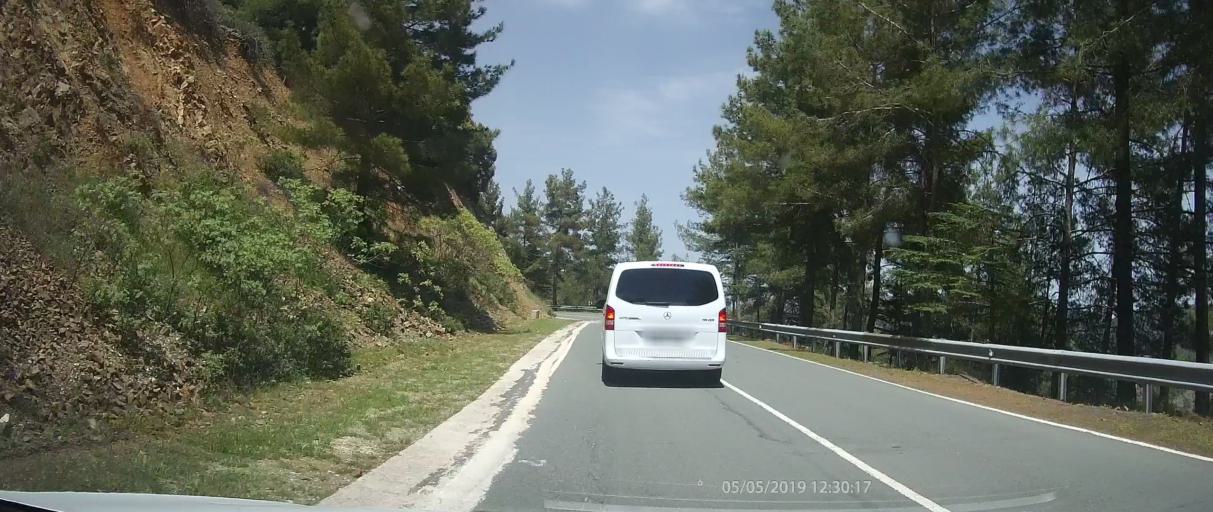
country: CY
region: Lefkosia
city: Kakopetria
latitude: 34.9831
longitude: 32.7492
